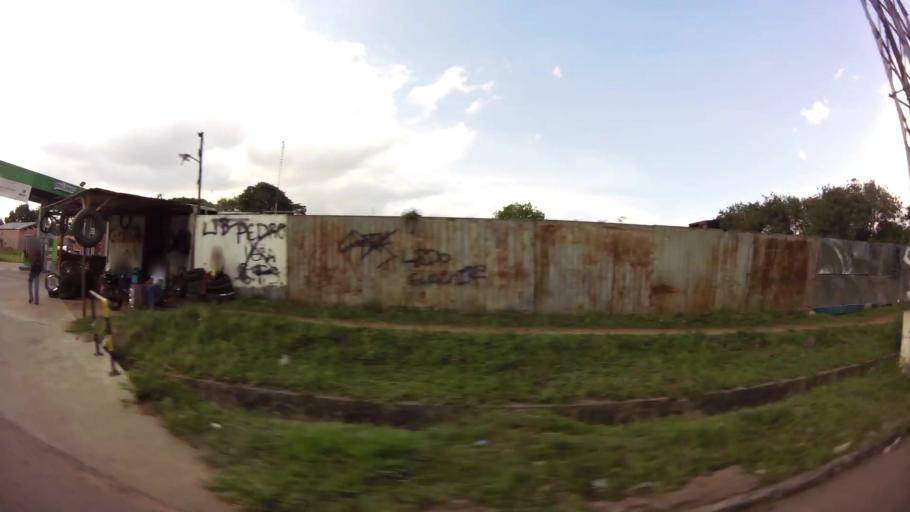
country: PY
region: Central
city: Villa Elisa
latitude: -25.3566
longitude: -57.5558
